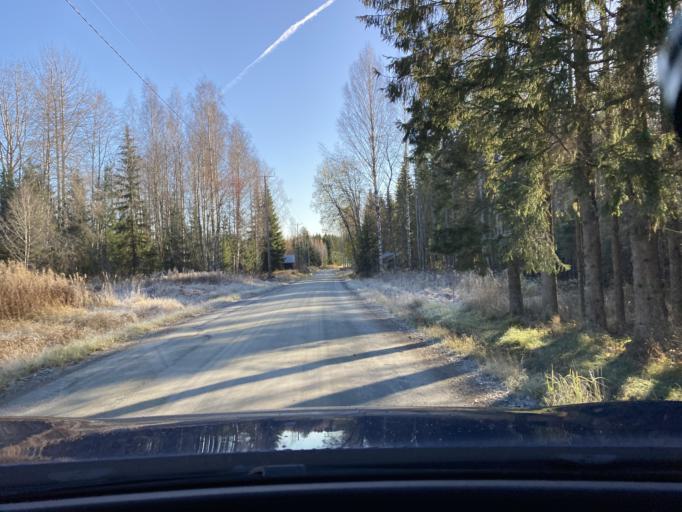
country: FI
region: Pirkanmaa
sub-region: Etelae-Pirkanmaa
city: Toijala
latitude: 61.0313
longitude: 23.7976
